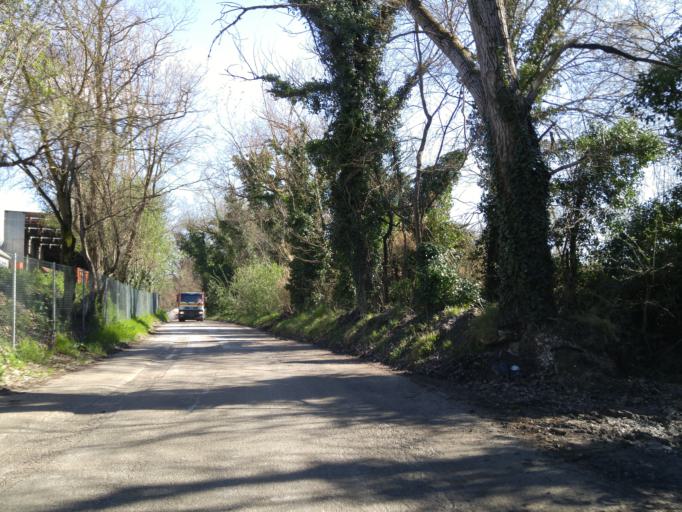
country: IT
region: The Marches
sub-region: Provincia di Pesaro e Urbino
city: Calcinelli
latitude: 43.7423
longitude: 12.9146
